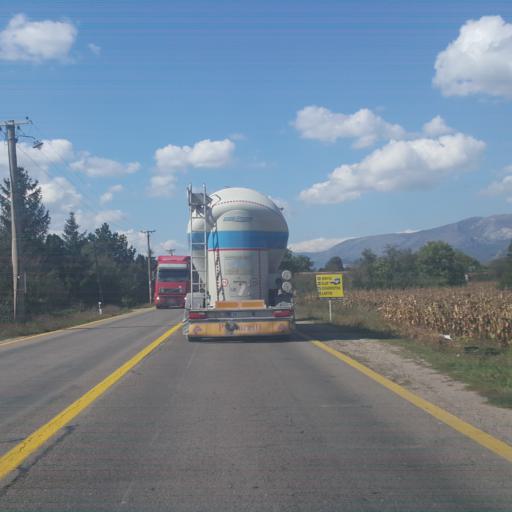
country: RS
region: Central Serbia
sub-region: Pirotski Okrug
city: Bela Palanka
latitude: 43.2649
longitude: 22.2509
